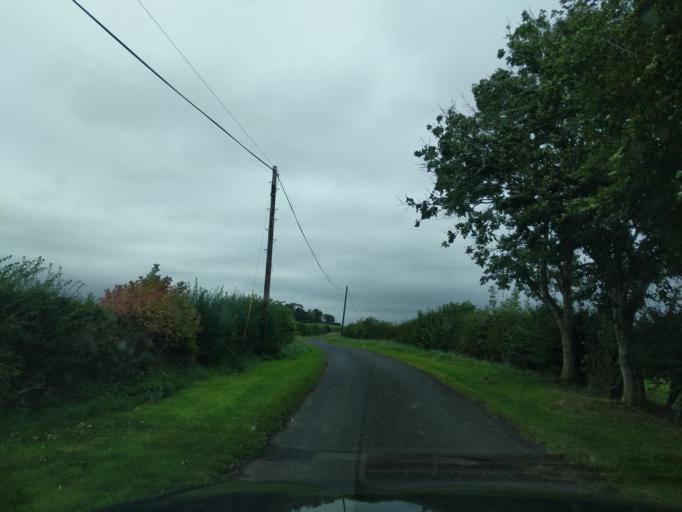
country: GB
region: Scotland
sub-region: The Scottish Borders
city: Kelso
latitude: 55.5928
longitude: -2.5220
